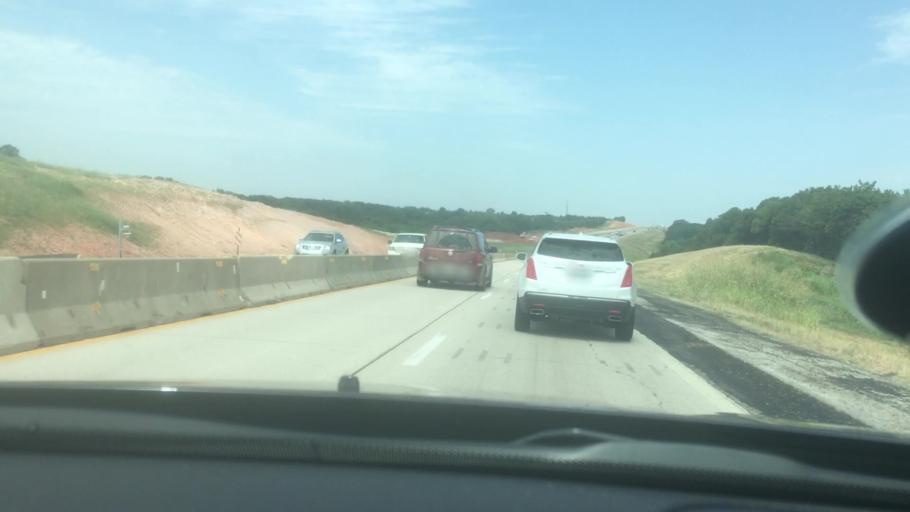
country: US
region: Oklahoma
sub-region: Oklahoma County
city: Choctaw
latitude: 35.3861
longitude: -97.2472
